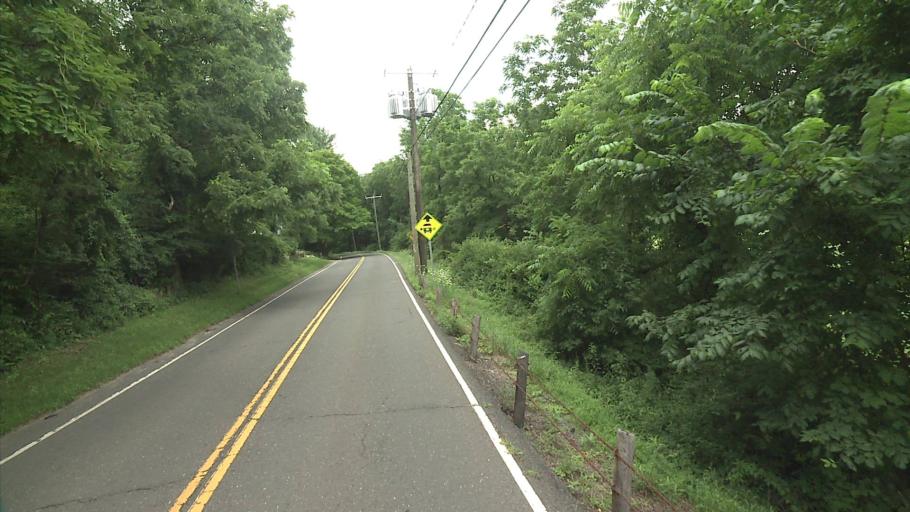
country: US
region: Connecticut
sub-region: Litchfield County
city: New Milford
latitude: 41.5512
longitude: -73.3294
